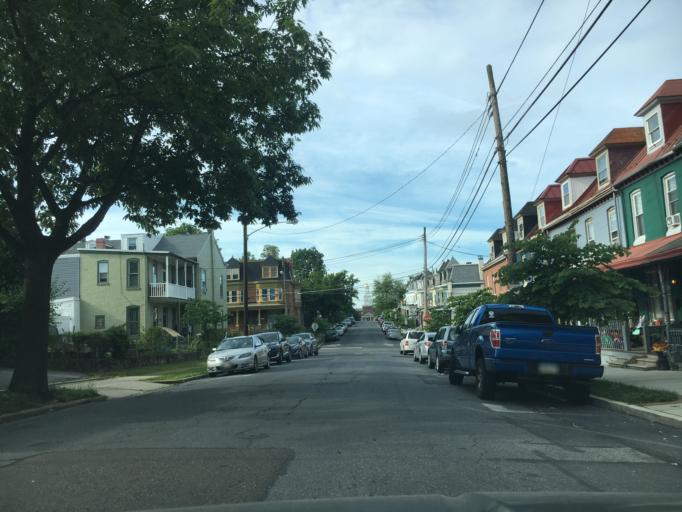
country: US
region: Pennsylvania
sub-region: Berks County
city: West Reading
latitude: 40.3353
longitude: -75.9498
